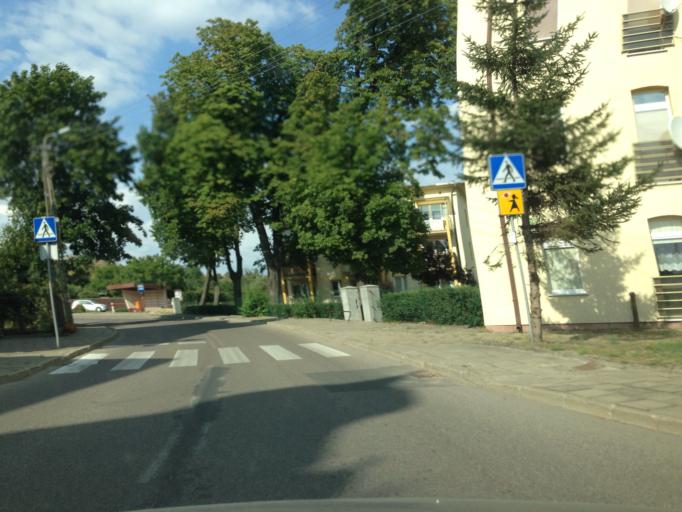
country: PL
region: Kujawsko-Pomorskie
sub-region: Powiat swiecki
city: Bukowiec
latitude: 53.3498
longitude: 18.3129
